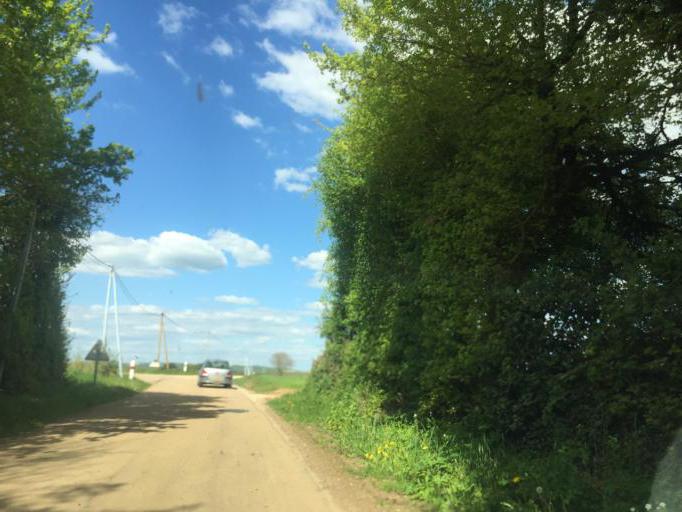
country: FR
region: Bourgogne
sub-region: Departement de l'Yonne
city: Fontenailles
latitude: 47.5671
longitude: 3.3443
